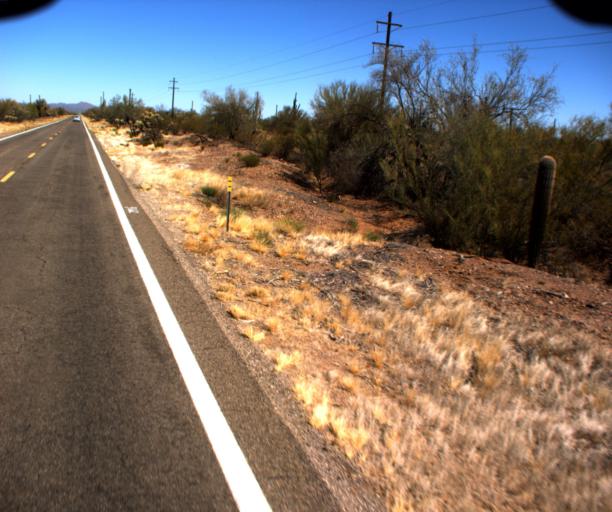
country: US
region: Arizona
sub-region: Pima County
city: Sells
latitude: 32.0440
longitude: -112.0205
